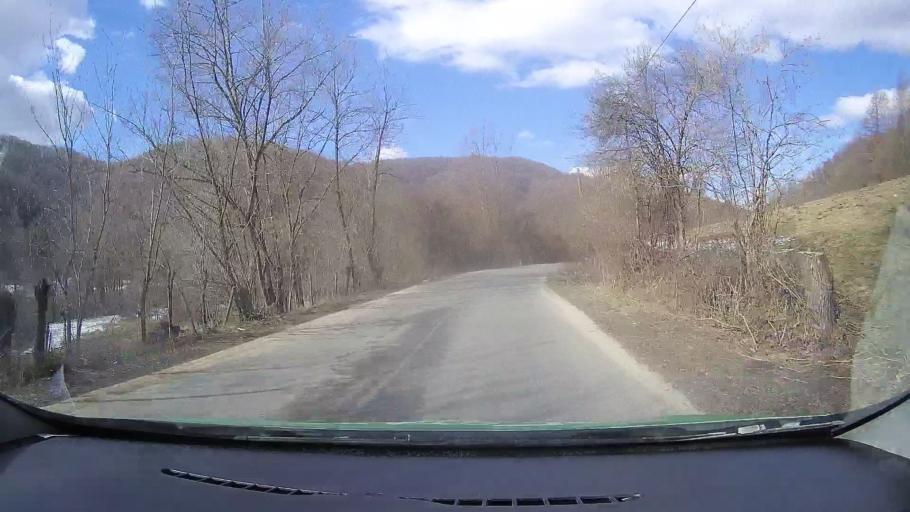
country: RO
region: Dambovita
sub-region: Comuna Vulcana Bai
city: Vulcana Bai
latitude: 45.0547
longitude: 25.3813
